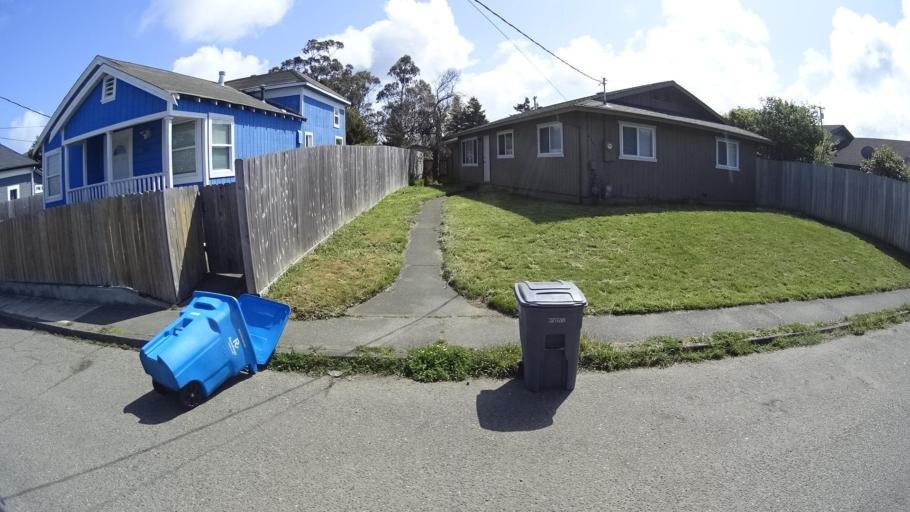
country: US
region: California
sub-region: Humboldt County
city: Bayview
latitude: 40.7699
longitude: -124.1820
